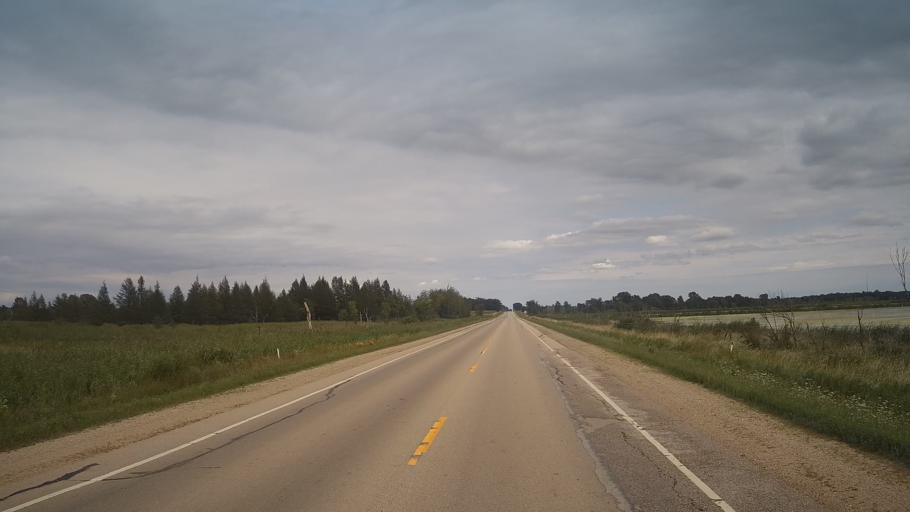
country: US
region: Wisconsin
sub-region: Green Lake County
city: Berlin
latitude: 44.0487
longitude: -88.9575
